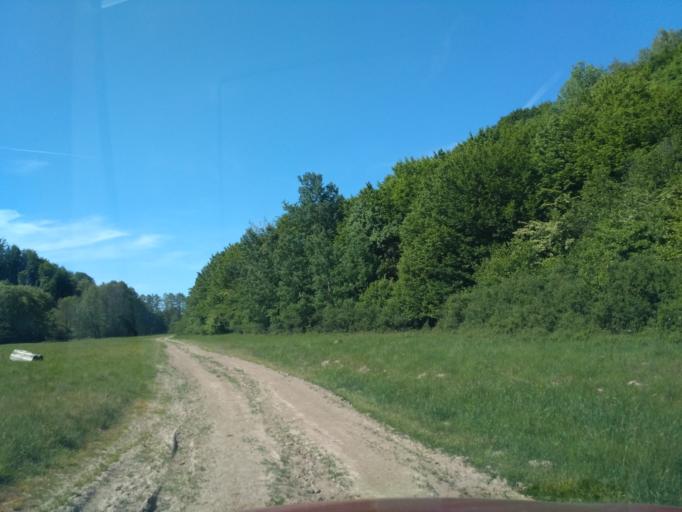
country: SK
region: Presovsky
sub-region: Okres Presov
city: Presov
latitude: 48.8878
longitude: 21.3938
